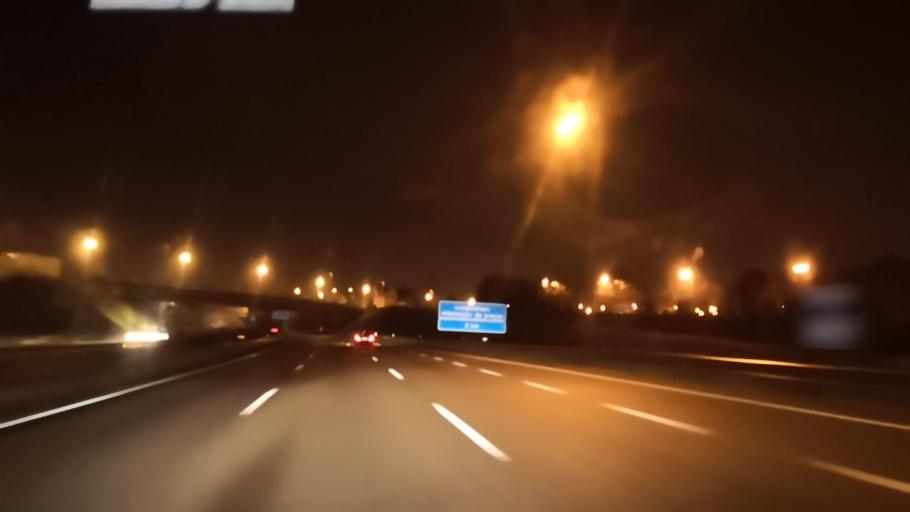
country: PT
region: Porto
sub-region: Maia
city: Leca do Bailio
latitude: 41.2020
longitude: -8.6167
